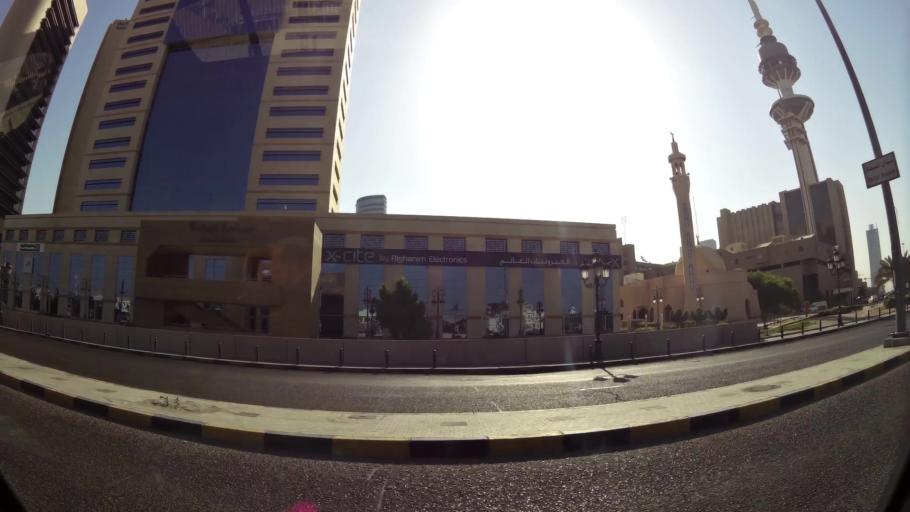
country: KW
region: Al Asimah
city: Kuwait City
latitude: 29.3712
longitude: 47.9739
